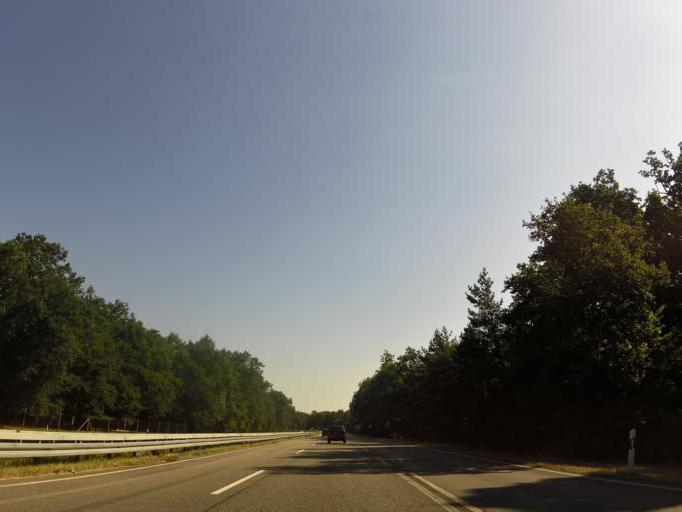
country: DE
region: Hesse
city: Niederrad
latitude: 50.0505
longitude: 8.6430
